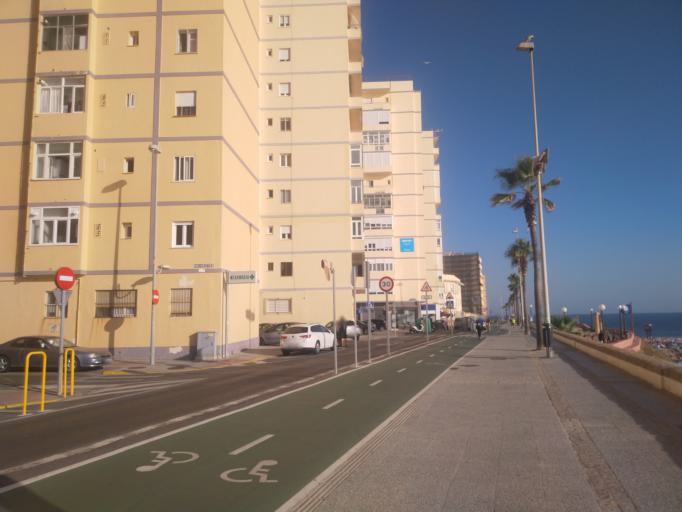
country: ES
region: Andalusia
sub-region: Provincia de Cadiz
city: Cadiz
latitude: 36.5200
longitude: -6.2863
